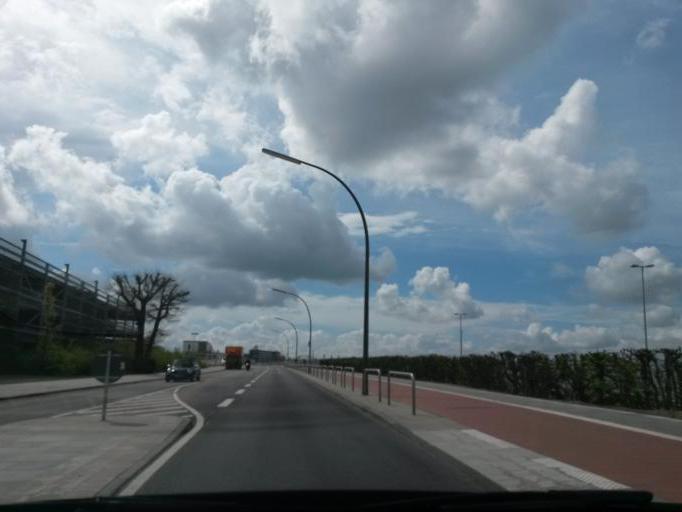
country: DE
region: Hamburg
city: Alsterdorf
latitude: 53.6231
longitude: 10.0073
